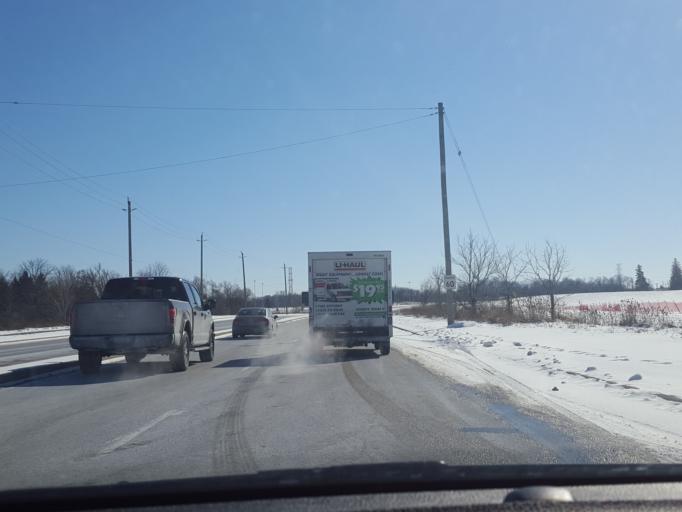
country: CA
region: Ontario
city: Waterloo
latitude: 43.4833
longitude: -80.5652
